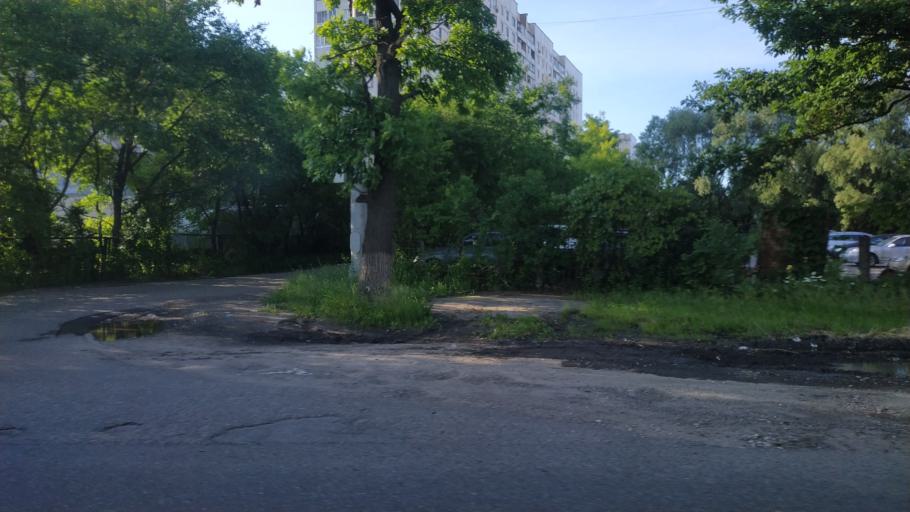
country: RU
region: Moskovskaya
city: Saltykovka
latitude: 55.7251
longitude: 37.9659
